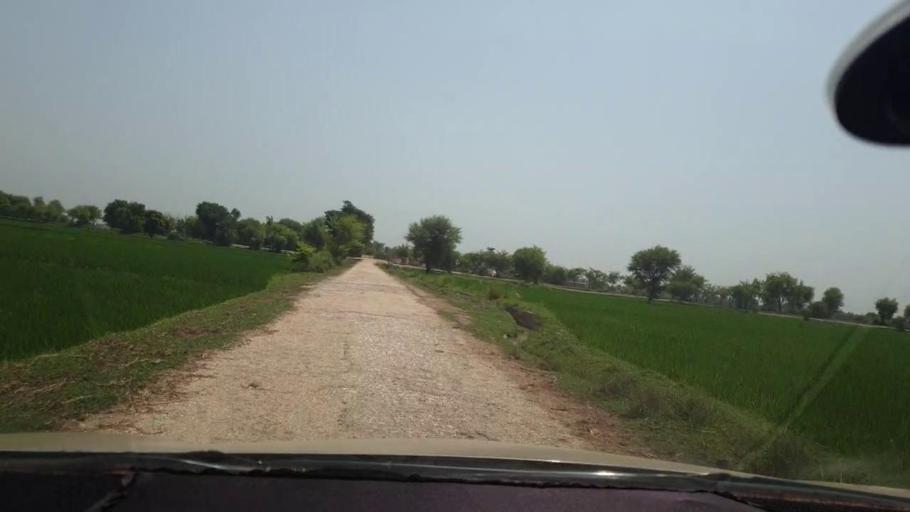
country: PK
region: Sindh
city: Kambar
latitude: 27.6395
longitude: 67.9330
